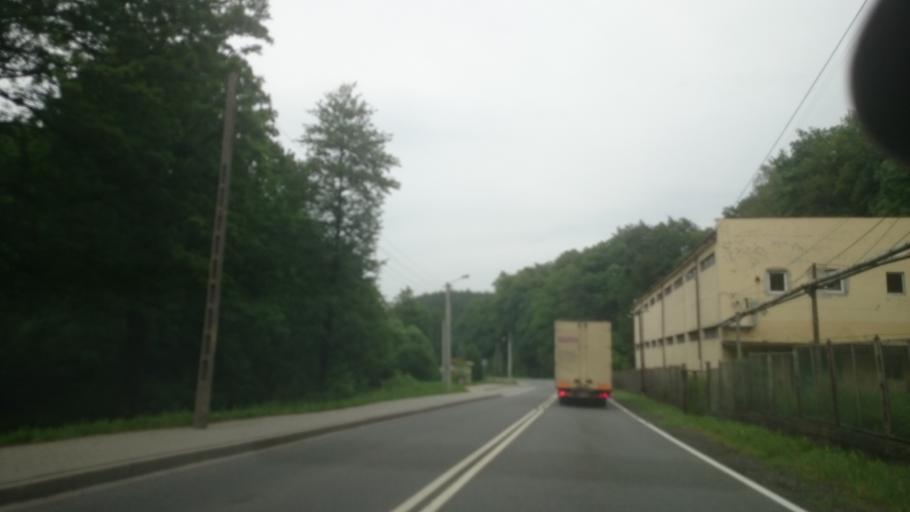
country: PL
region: Lower Silesian Voivodeship
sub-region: Powiat zabkowicki
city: Zloty Stok
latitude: 50.4451
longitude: 16.8348
